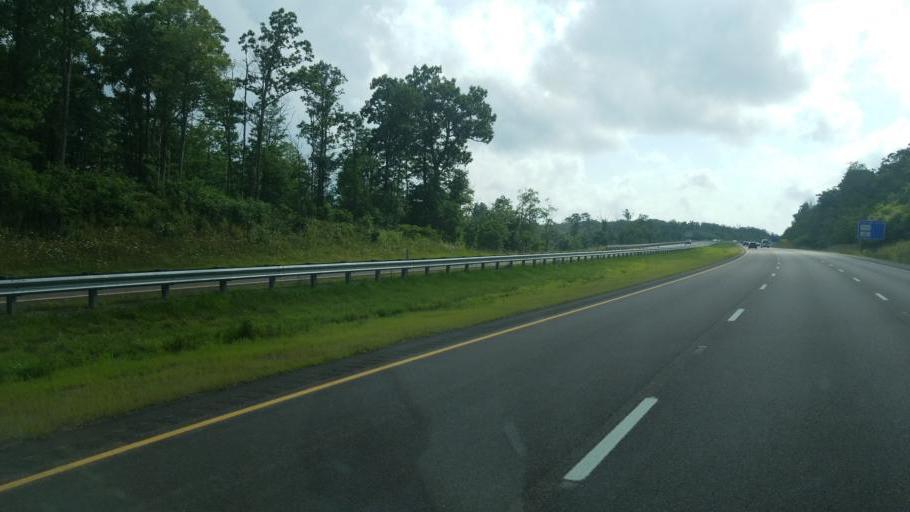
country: US
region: Pennsylvania
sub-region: Somerset County
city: Meyersdale
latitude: 39.6838
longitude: -79.2082
